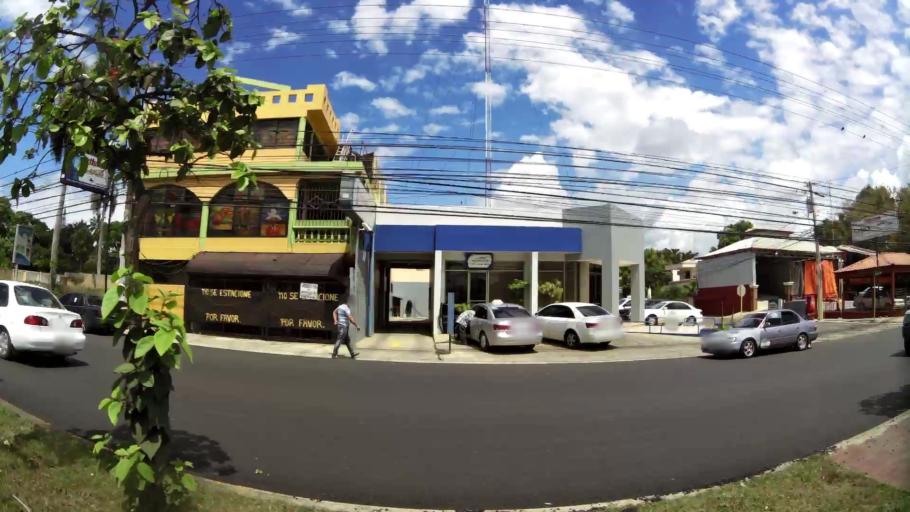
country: DO
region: Santiago
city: Santiago de los Caballeros
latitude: 19.4586
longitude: -70.6732
